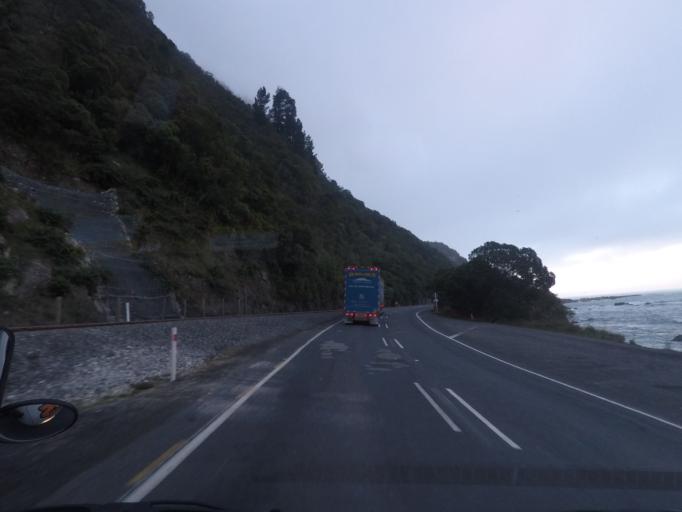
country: NZ
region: Canterbury
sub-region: Kaikoura District
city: Kaikoura
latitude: -42.4508
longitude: 173.5694
